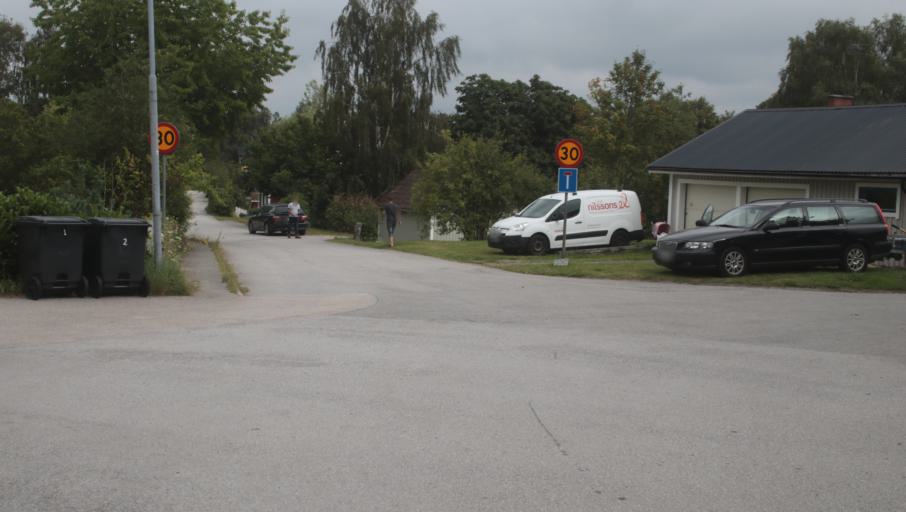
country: SE
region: Blekinge
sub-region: Karlshamns Kommun
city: Karlshamn
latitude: 56.2133
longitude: 14.9500
